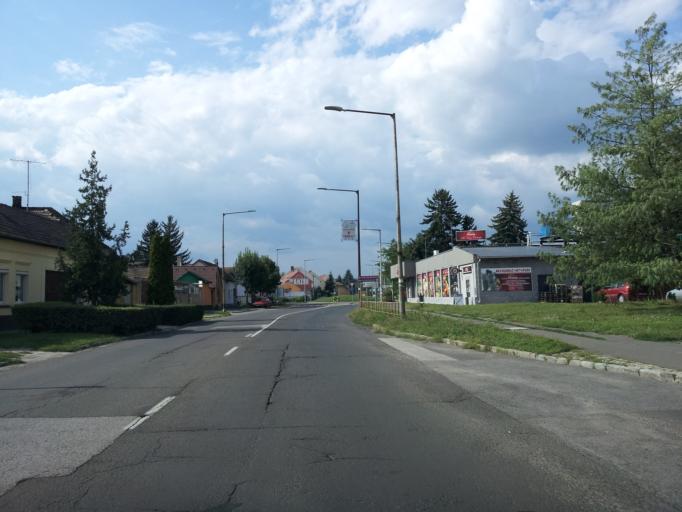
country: HU
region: Pest
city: Vac
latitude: 47.7905
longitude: 19.1173
